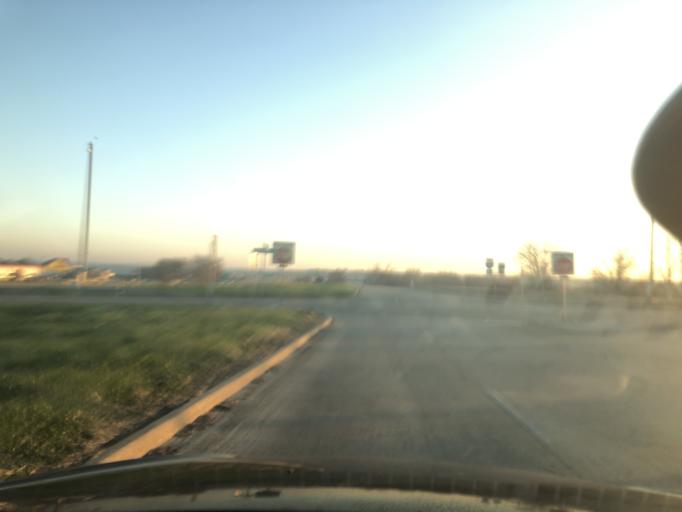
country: US
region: Texas
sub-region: Tarrant County
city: White Settlement
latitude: 32.7337
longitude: -97.4825
